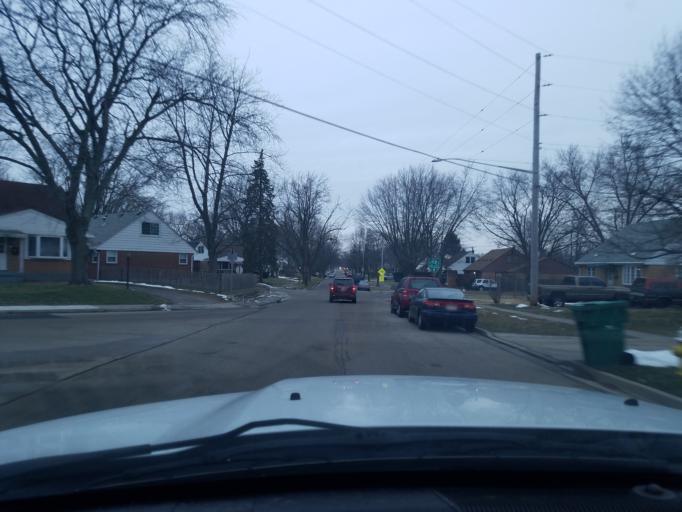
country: US
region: Ohio
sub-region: Montgomery County
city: Kettering
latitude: 39.7092
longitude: -84.1517
